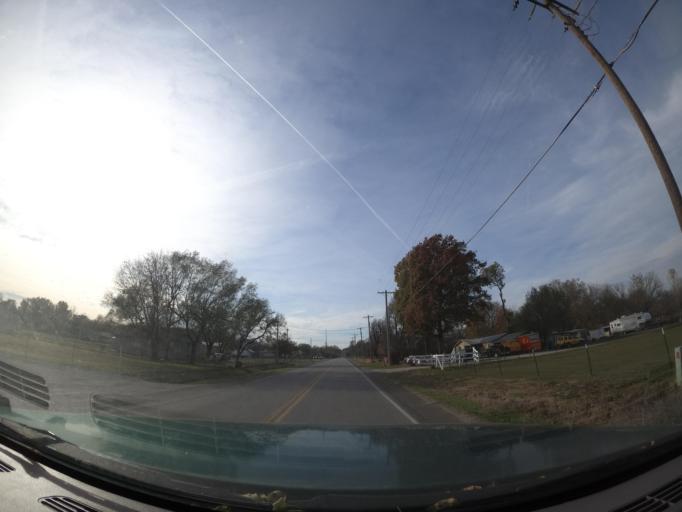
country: US
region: Oklahoma
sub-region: Tulsa County
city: Turley
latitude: 36.2496
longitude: -95.9666
